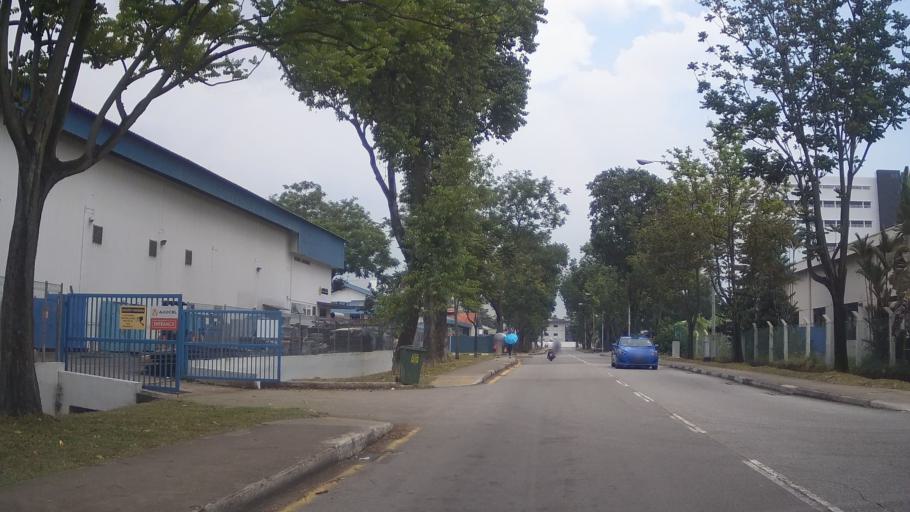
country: MY
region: Johor
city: Johor Bahru
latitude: 1.3292
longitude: 103.7009
